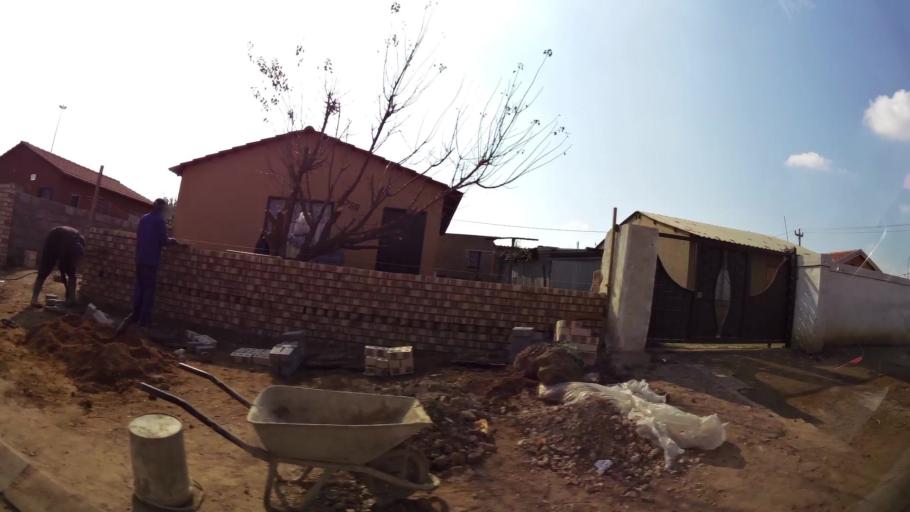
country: ZA
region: Gauteng
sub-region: Ekurhuleni Metropolitan Municipality
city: Springs
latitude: -26.1093
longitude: 28.4772
